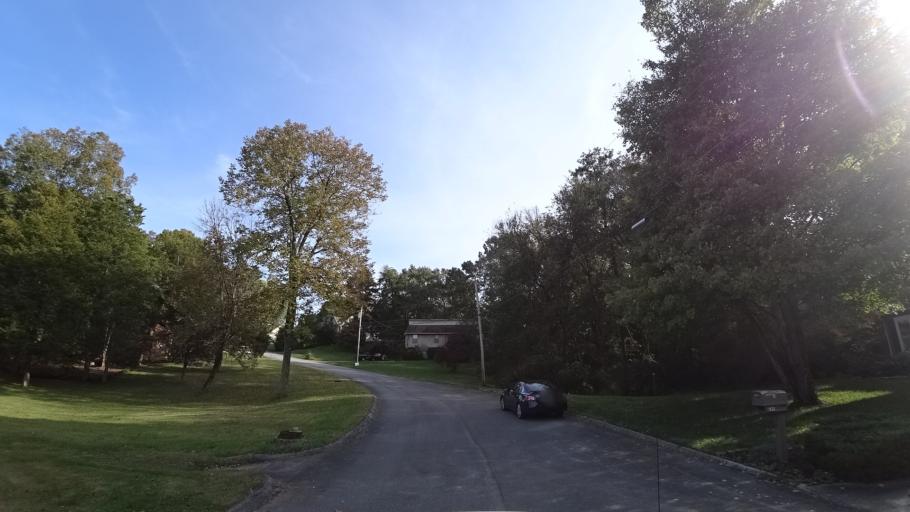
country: US
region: Tennessee
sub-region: Knox County
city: Farragut
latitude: 35.9051
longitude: -84.1642
